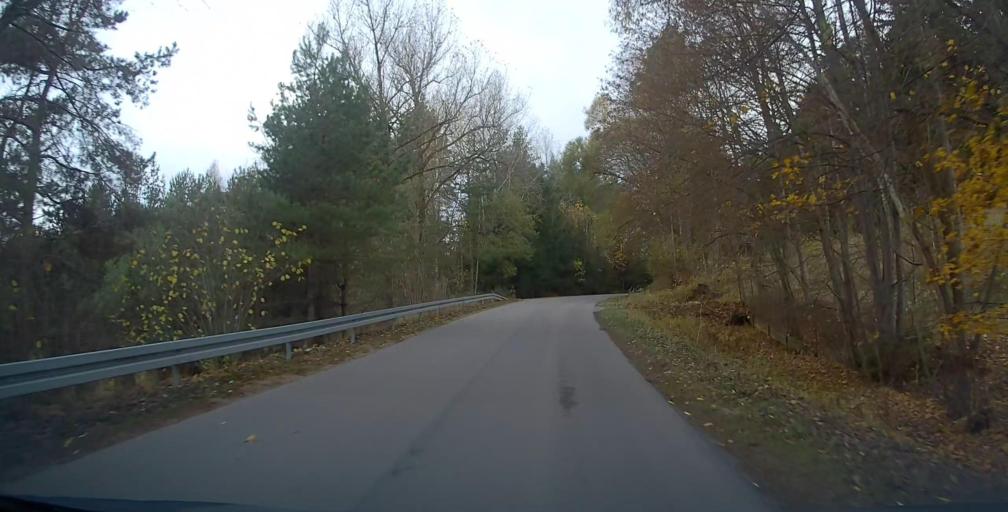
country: PL
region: Podlasie
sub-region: Suwalki
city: Suwalki
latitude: 54.2847
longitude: 22.8919
